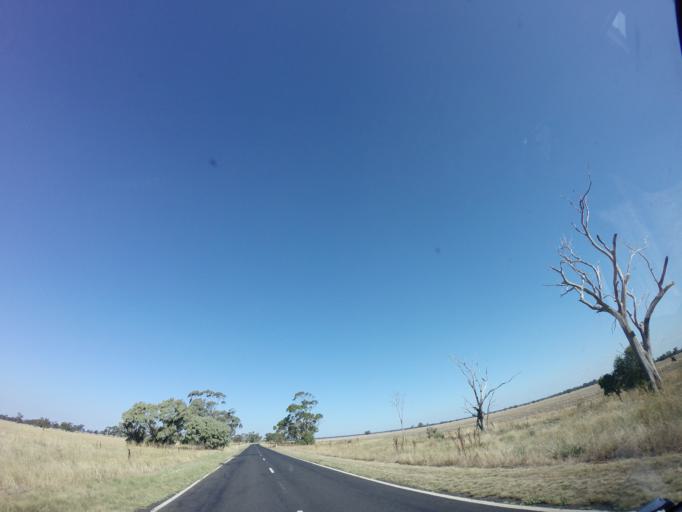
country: AU
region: New South Wales
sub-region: Gilgandra
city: Gilgandra
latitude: -31.7030
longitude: 148.5908
